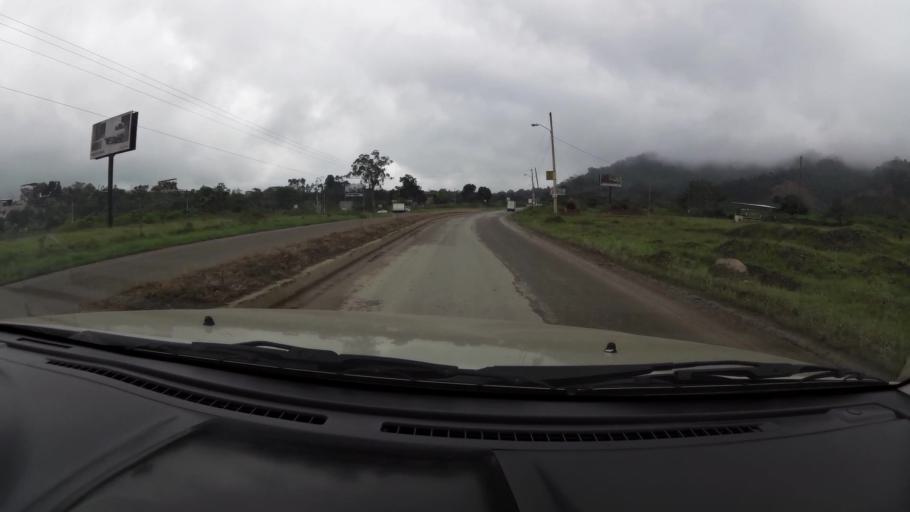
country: EC
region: El Oro
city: Pasaje
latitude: -3.3282
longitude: -79.7729
